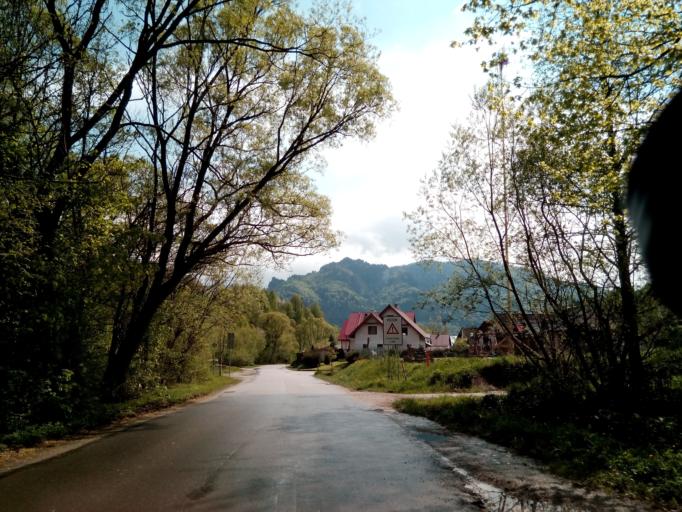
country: SK
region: Zilinsky
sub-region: Okres Zilina
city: Terchova
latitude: 49.2703
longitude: 19.0369
